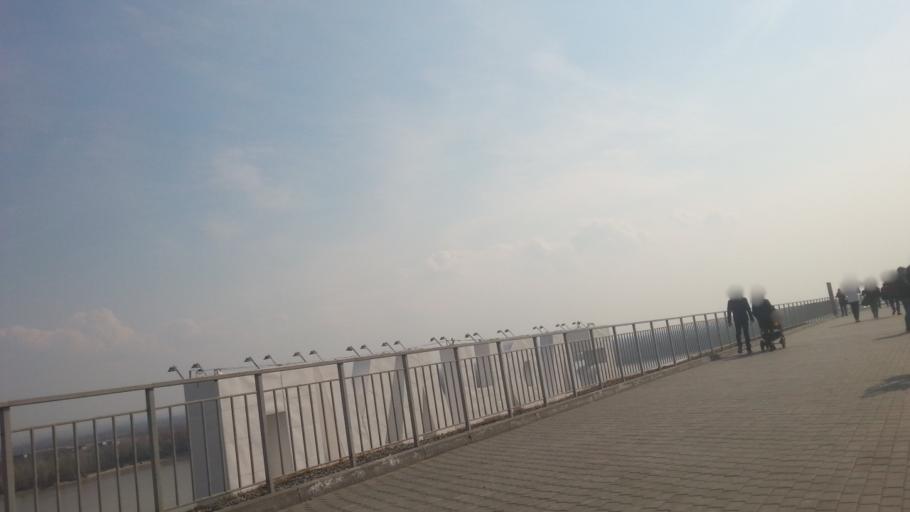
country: RU
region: Altai Krai
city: Zaton
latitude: 53.3237
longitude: 83.7966
